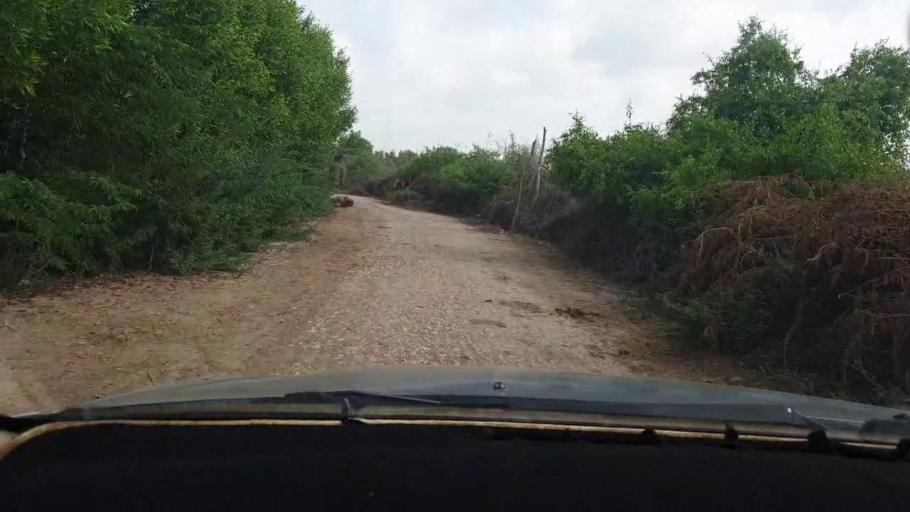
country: PK
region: Sindh
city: Tando Bago
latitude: 24.7696
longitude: 69.0237
